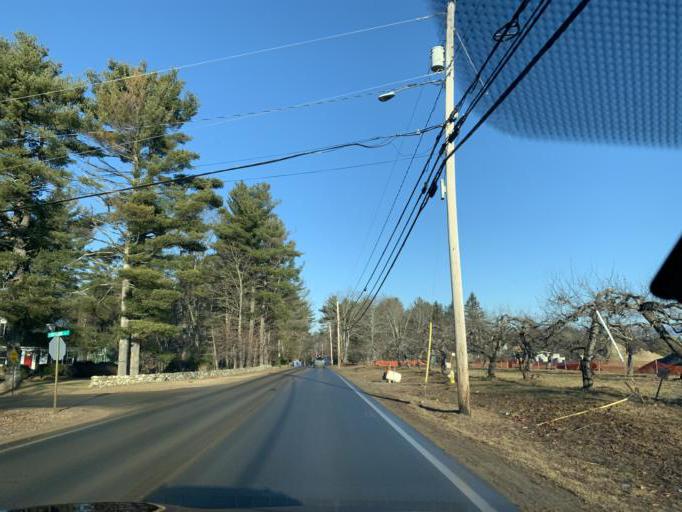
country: US
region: New Hampshire
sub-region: Rockingham County
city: Londonderry
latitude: 42.8697
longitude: -71.3553
